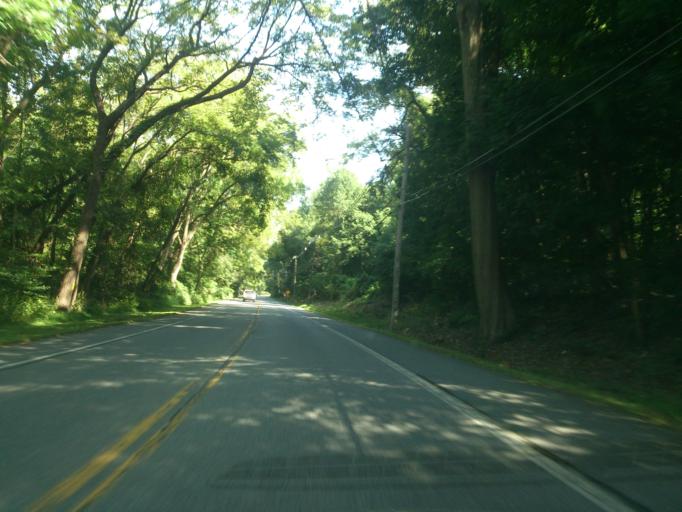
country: US
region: Pennsylvania
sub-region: Lebanon County
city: Cornwall
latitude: 40.2750
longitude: -76.4227
